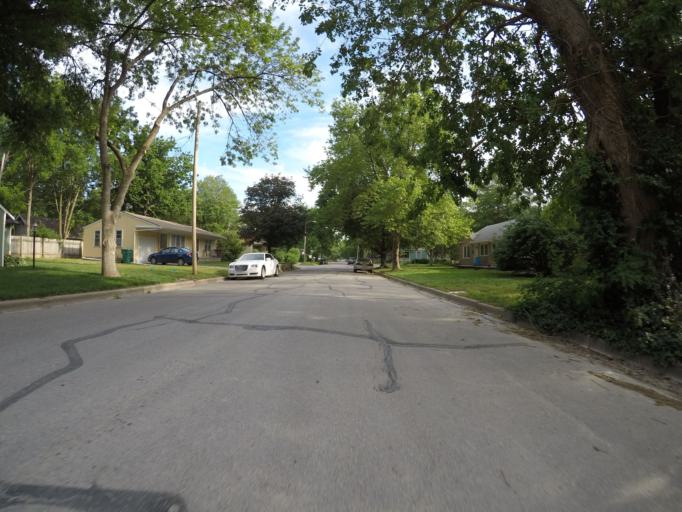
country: US
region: Kansas
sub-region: Riley County
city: Manhattan
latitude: 39.1893
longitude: -96.5633
